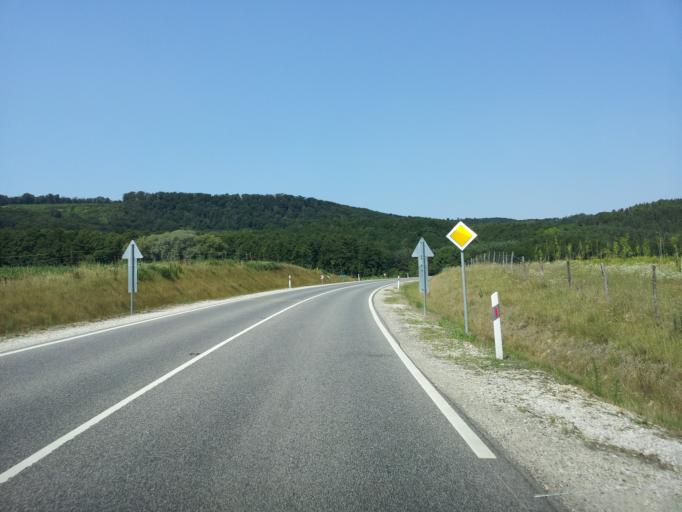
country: HU
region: Zala
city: Zalaegerszeg
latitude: 46.8272
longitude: 16.9336
